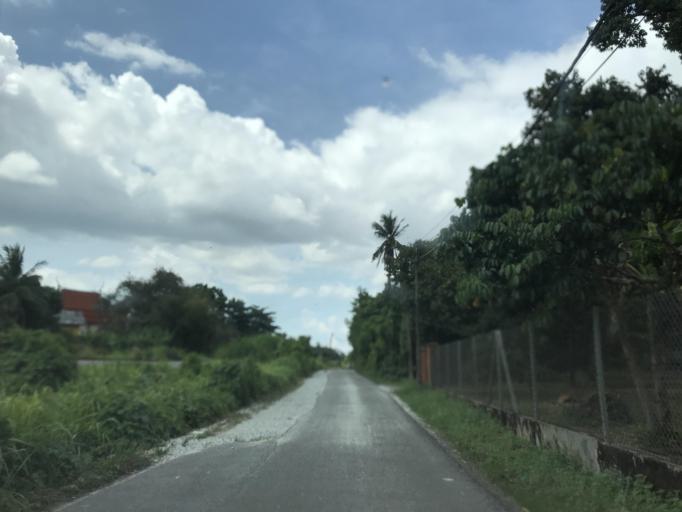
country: MY
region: Kelantan
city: Kota Bharu
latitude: 6.1116
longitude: 102.1933
